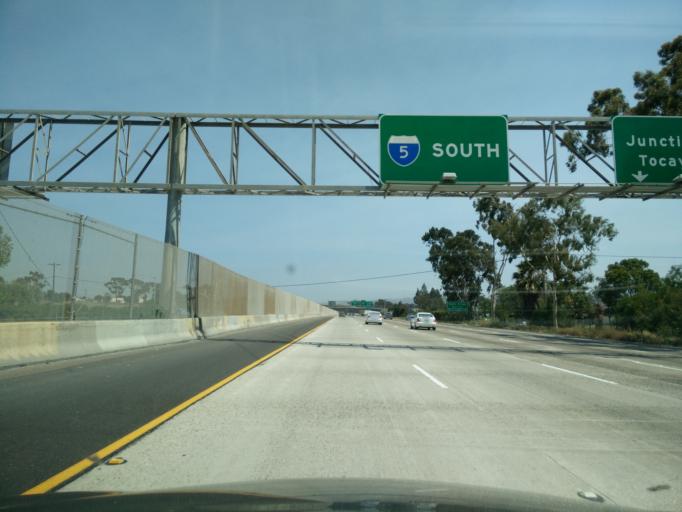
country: US
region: California
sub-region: San Diego County
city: Imperial Beach
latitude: 32.5736
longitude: -117.0801
